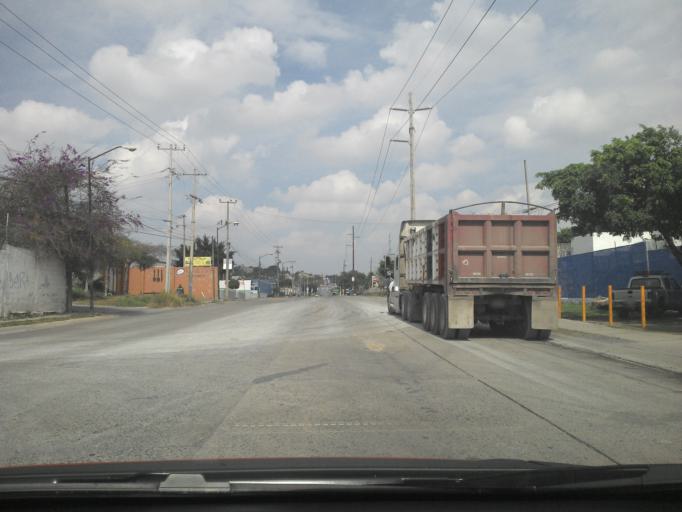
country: MX
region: Jalisco
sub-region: Tlajomulco de Zuniga
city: Altus Bosques
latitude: 20.5808
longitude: -103.3556
